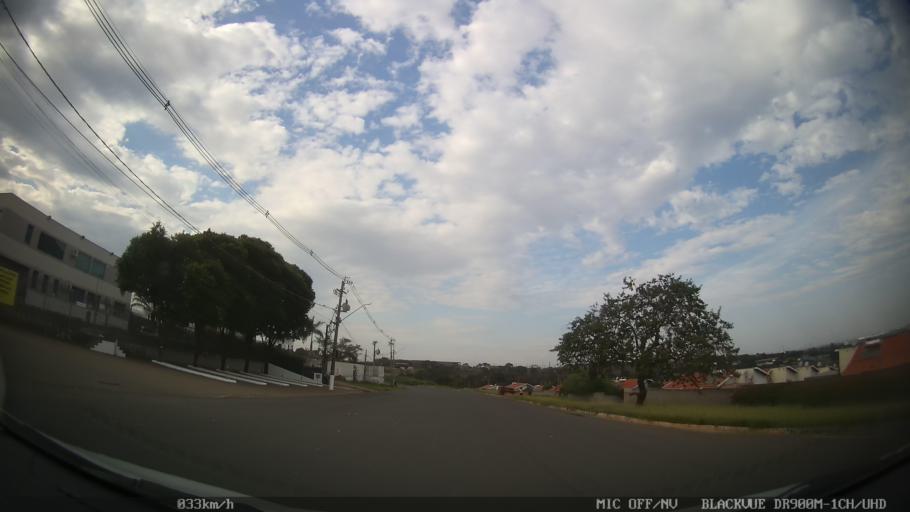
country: BR
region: Sao Paulo
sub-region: Paulinia
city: Paulinia
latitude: -22.7372
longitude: -47.1672
